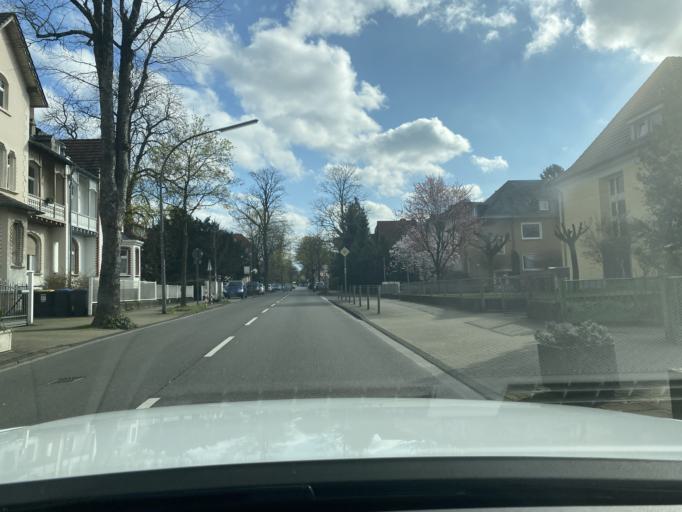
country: DE
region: North Rhine-Westphalia
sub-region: Regierungsbezirk Koln
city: Merheim
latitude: 50.9818
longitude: 7.0824
